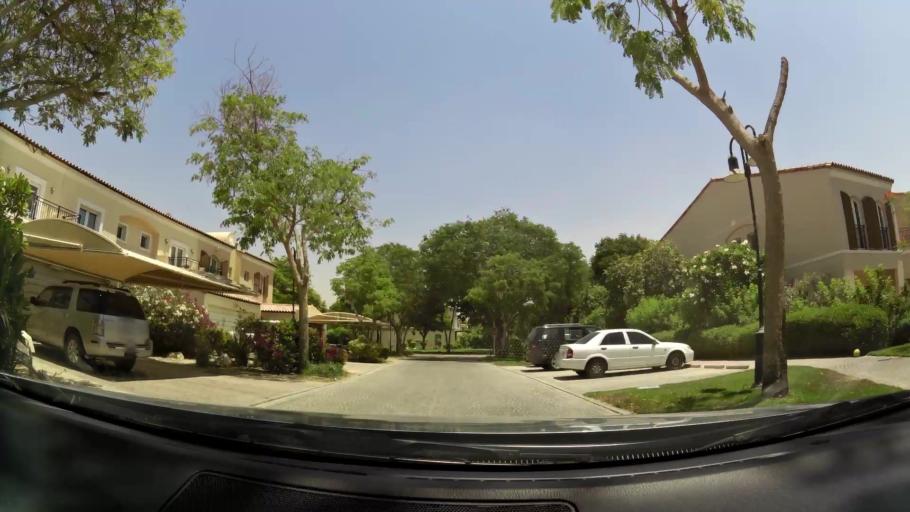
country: AE
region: Dubai
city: Dubai
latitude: 25.0080
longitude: 55.1583
